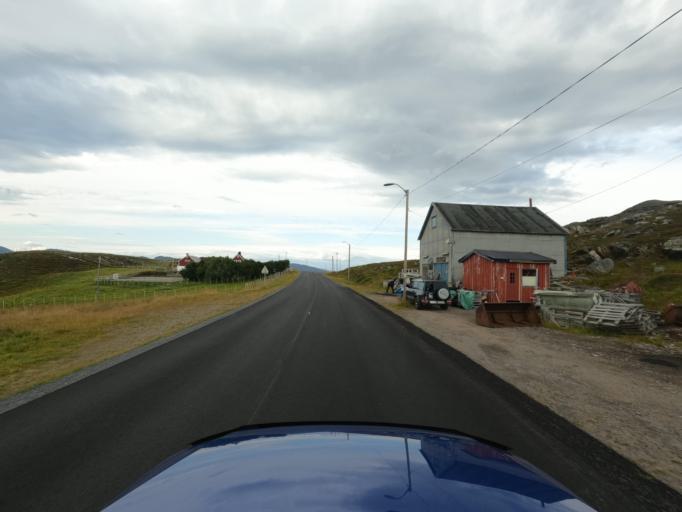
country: NO
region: Finnmark Fylke
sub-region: Hammerfest
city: Rypefjord
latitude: 70.5474
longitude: 23.7287
